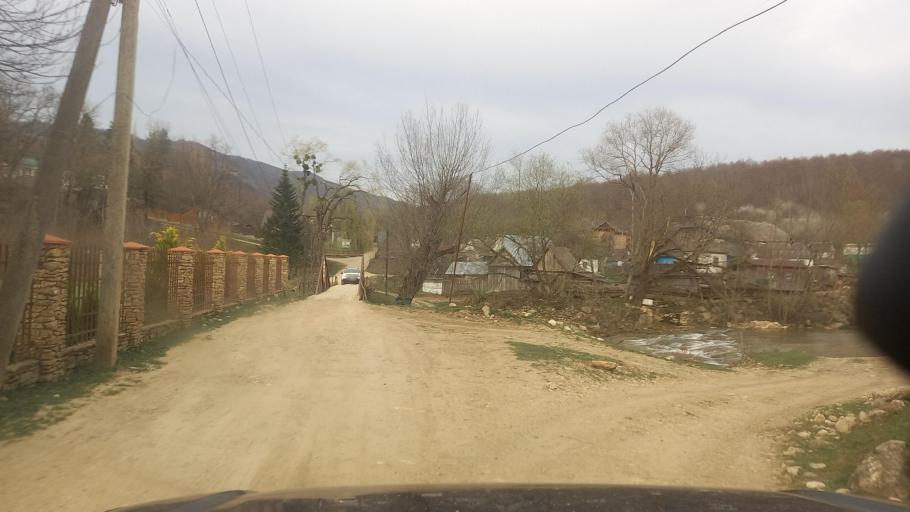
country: RU
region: Adygeya
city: Kamennomostskiy
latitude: 44.1978
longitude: 39.9624
